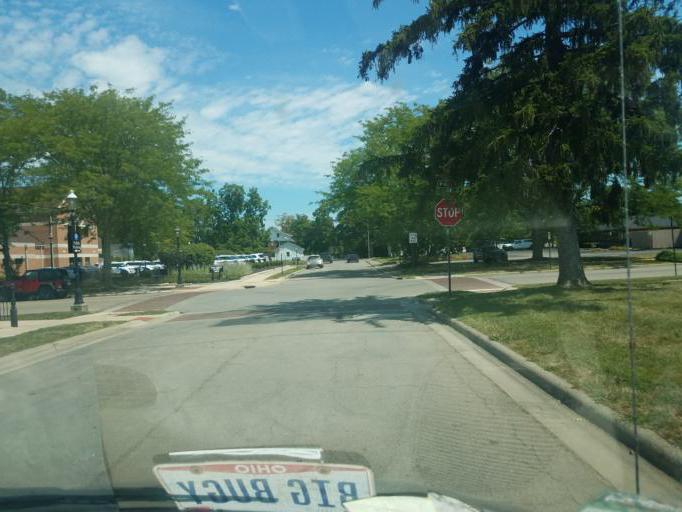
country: US
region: Ohio
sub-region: Franklin County
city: Grove City
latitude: 39.8812
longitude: -83.0922
